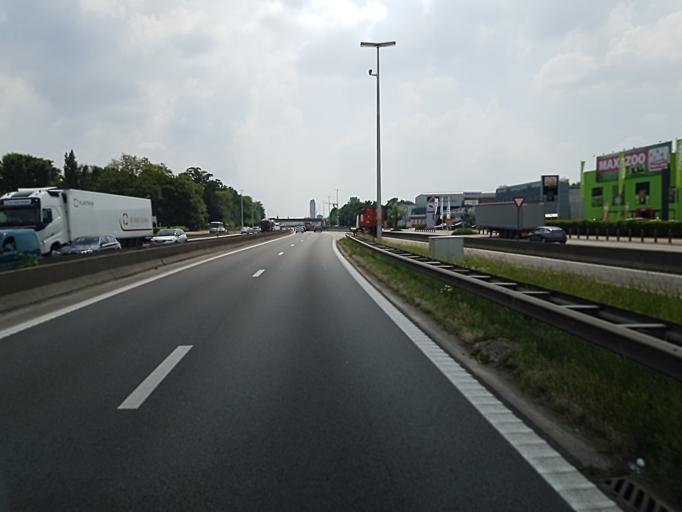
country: BE
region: Flanders
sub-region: Provincie Antwerpen
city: Boom
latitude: 51.1155
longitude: 4.3719
